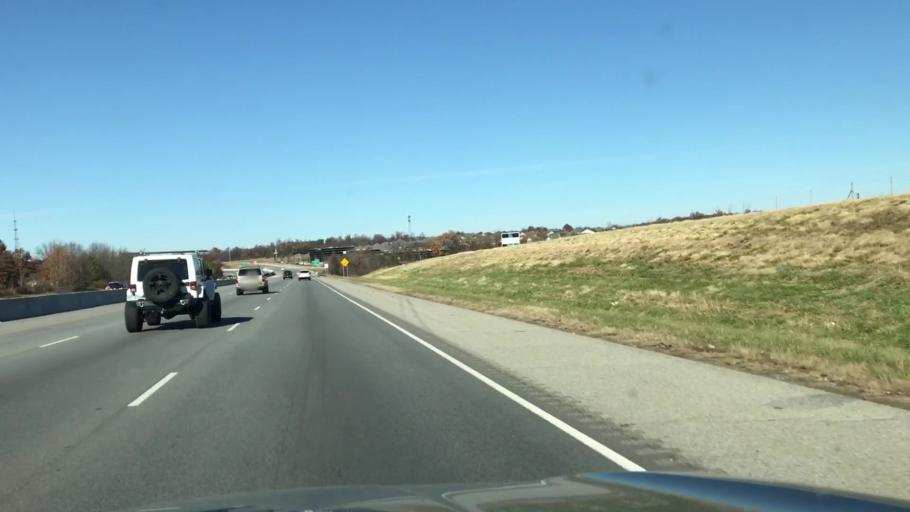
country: US
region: Arkansas
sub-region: Benton County
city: Lowell
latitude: 36.2893
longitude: -94.1615
